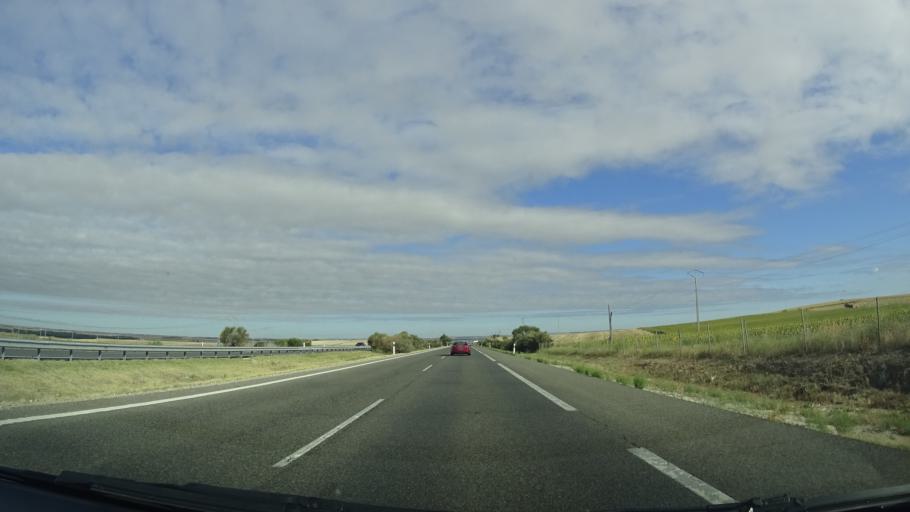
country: ES
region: Castille and Leon
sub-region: Provincia de Valladolid
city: San Vicente del Palacio
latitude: 41.2040
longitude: -4.8260
